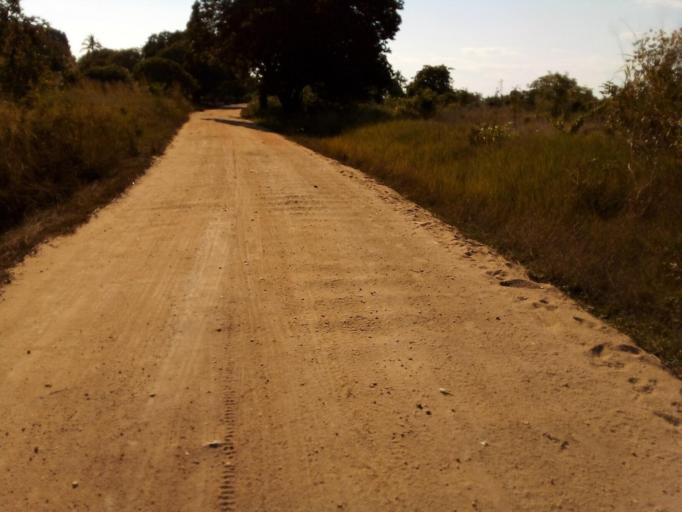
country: MZ
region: Zambezia
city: Quelimane
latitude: -17.5381
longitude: 36.6237
